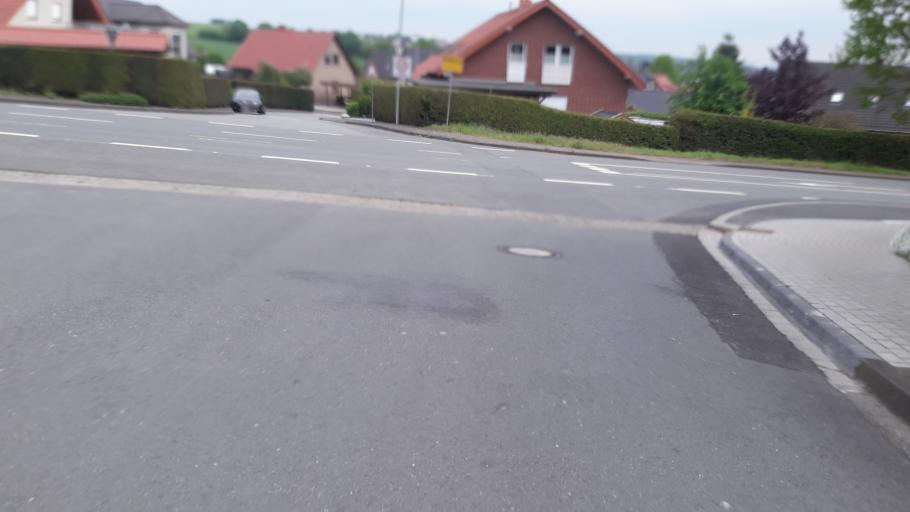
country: DE
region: North Rhine-Westphalia
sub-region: Regierungsbezirk Detmold
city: Paderborn
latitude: 51.6758
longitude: 8.7309
